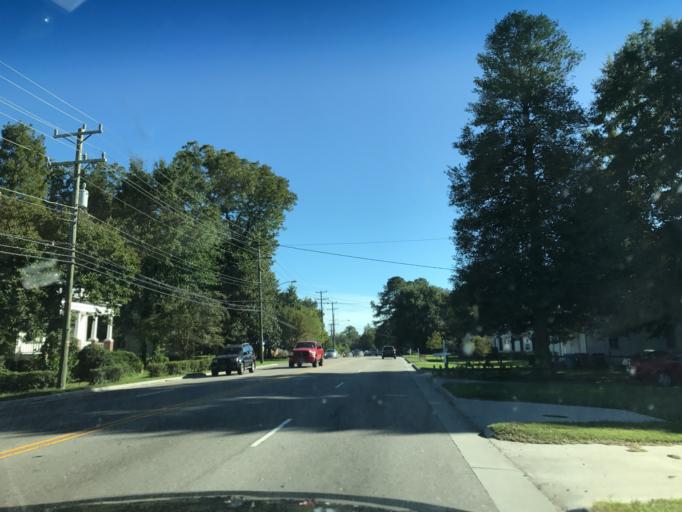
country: US
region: Virginia
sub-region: City of Portsmouth
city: Portsmouth Heights
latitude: 36.7495
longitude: -76.3461
